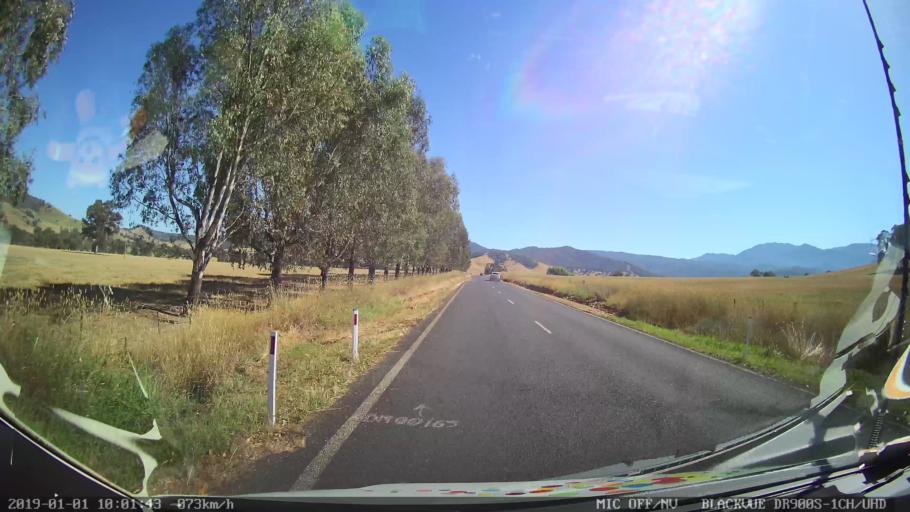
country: AU
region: New South Wales
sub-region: Snowy River
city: Jindabyne
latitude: -36.1886
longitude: 148.1007
